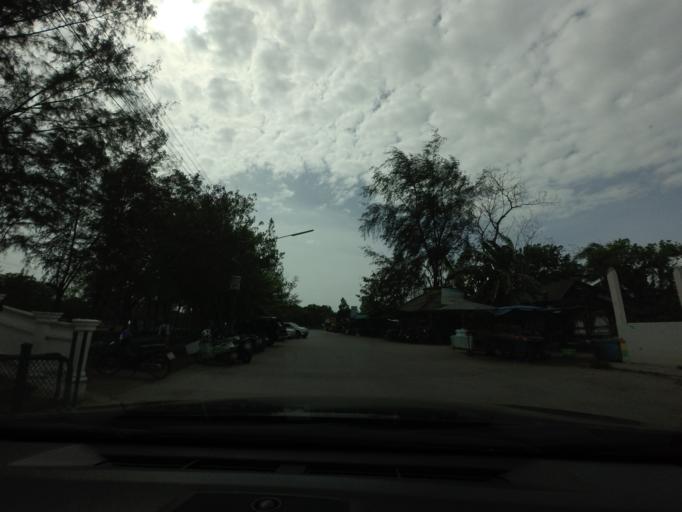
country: TH
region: Pattani
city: Pattani
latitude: 6.8948
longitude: 101.2460
